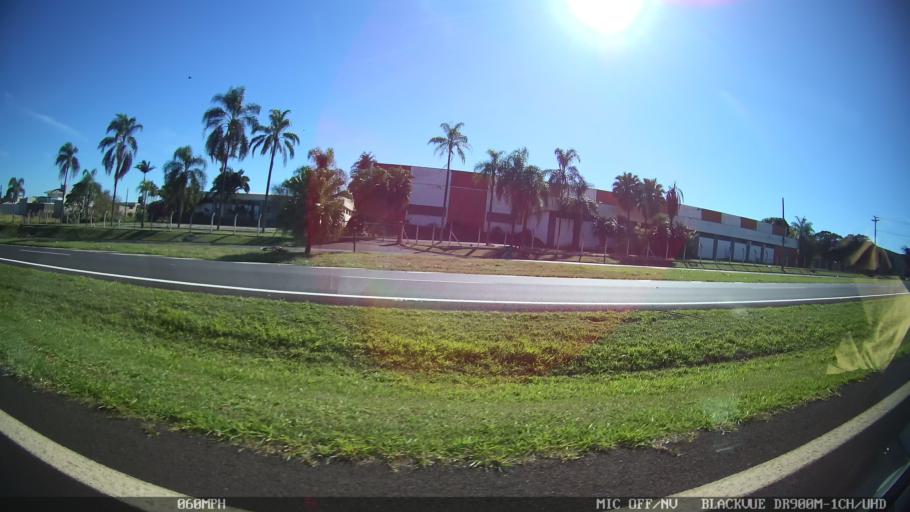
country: BR
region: Sao Paulo
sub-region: Franca
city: Franca
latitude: -20.5703
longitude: -47.3940
